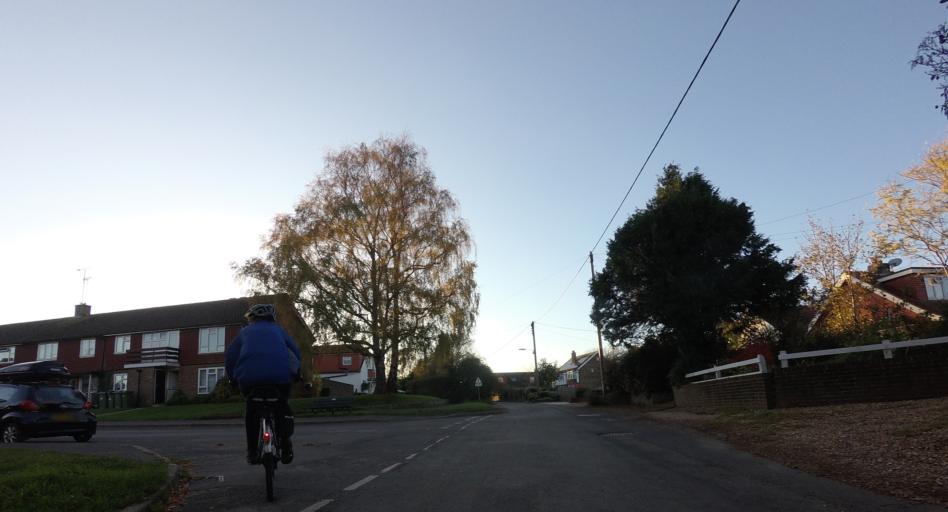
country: GB
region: England
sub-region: West Sussex
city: Steyning
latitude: 50.8902
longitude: -0.3141
